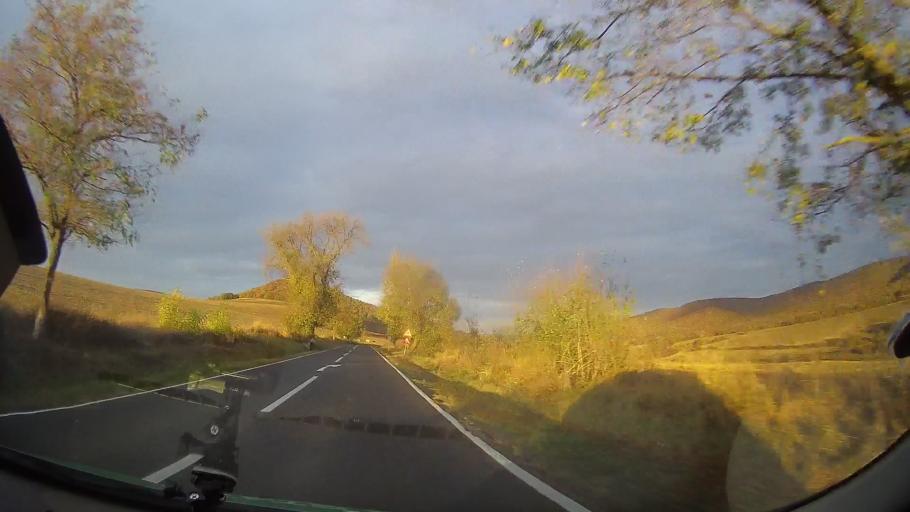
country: RO
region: Tulcea
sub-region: Comuna Ciucurova
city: Ciucurova
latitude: 44.9439
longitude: 28.4957
